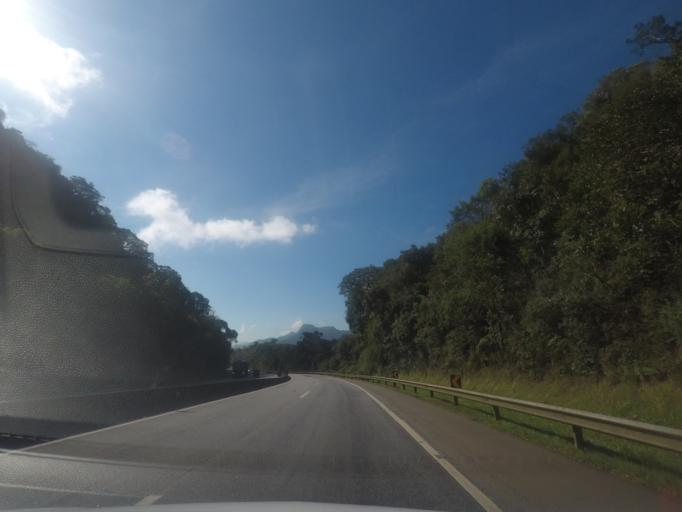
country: BR
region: Parana
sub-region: Piraquara
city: Piraquara
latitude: -25.5914
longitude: -48.9289
